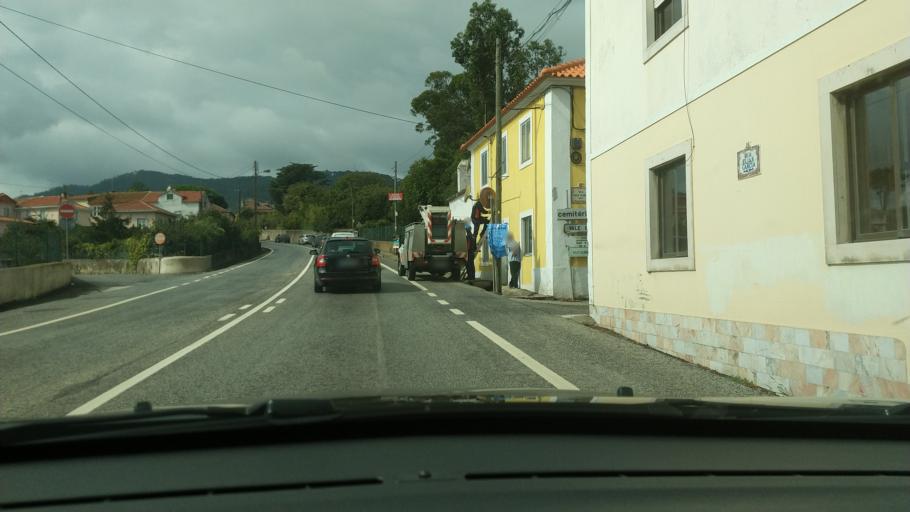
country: PT
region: Lisbon
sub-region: Sintra
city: Sintra
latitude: 38.7837
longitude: -9.3662
